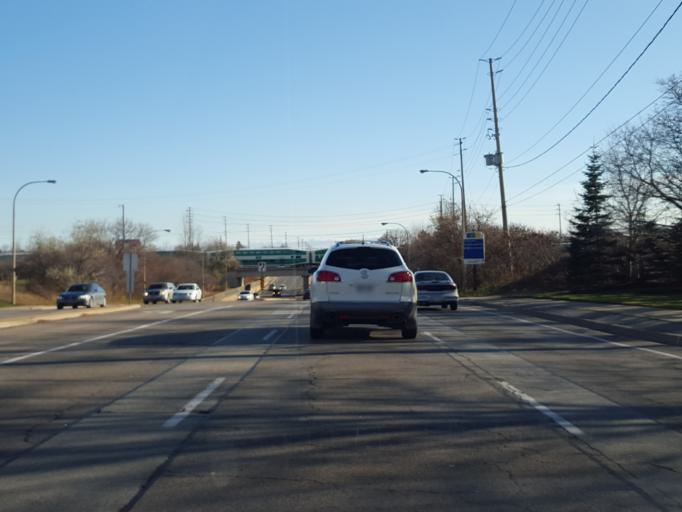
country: CA
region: Ontario
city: Burlington
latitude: 43.3622
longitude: -79.7825
